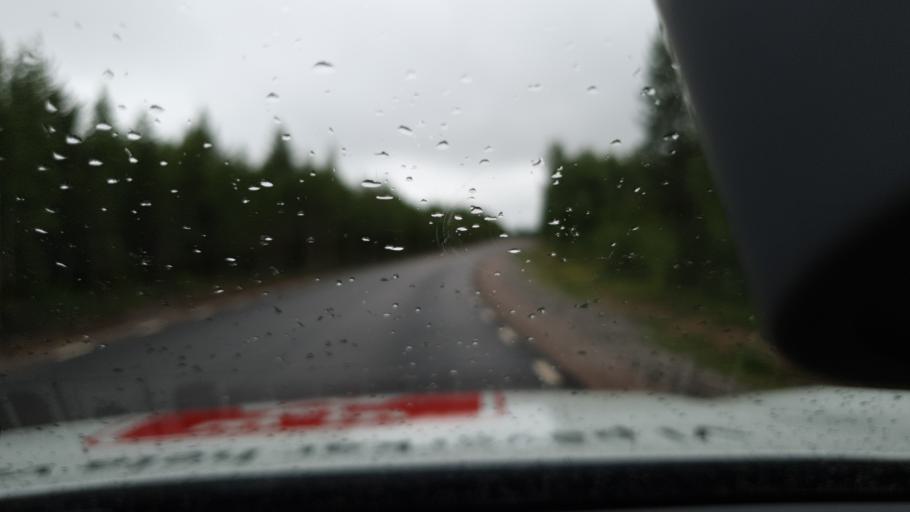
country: SE
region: Norrbotten
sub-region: Overtornea Kommun
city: OEvertornea
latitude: 66.4655
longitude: 23.4685
